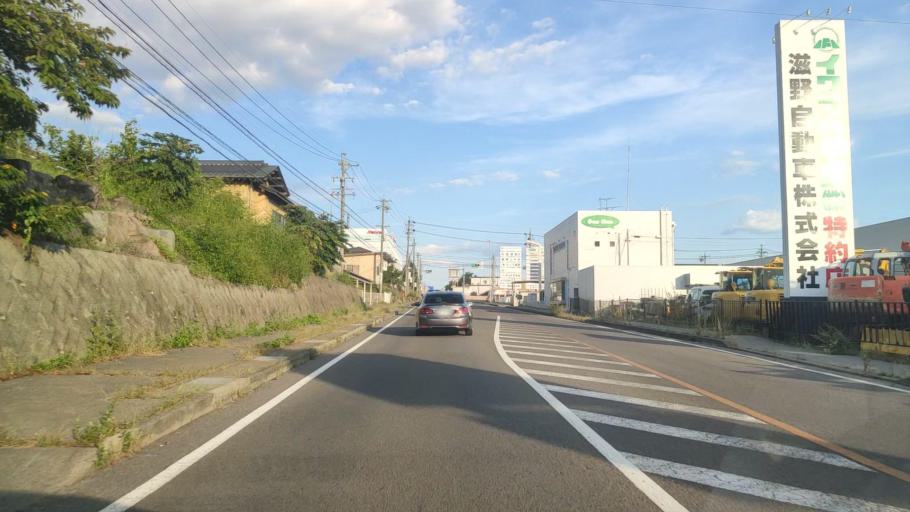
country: JP
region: Nagano
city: Komoro
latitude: 36.3510
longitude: 138.3568
